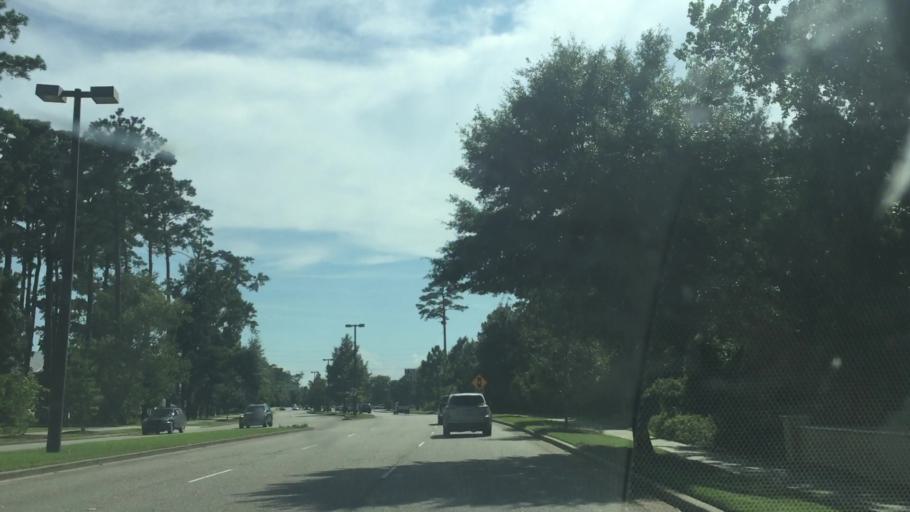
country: US
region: South Carolina
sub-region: Horry County
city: Myrtle Beach
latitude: 33.7176
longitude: -78.8711
